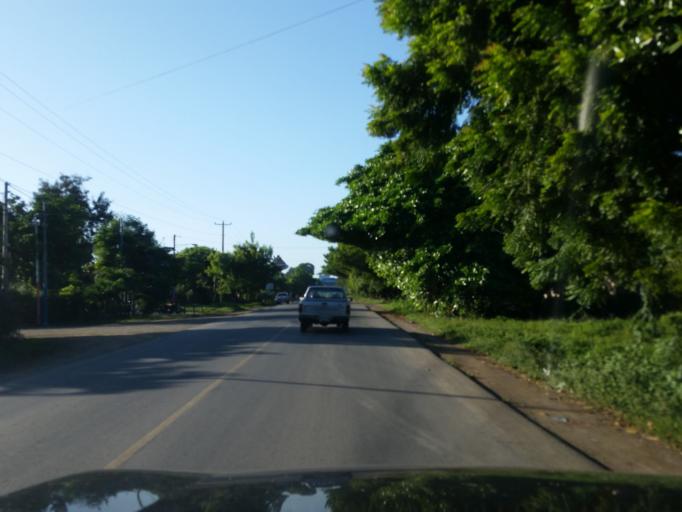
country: NI
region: Rivas
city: Rivas
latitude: 11.4480
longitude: -85.8313
